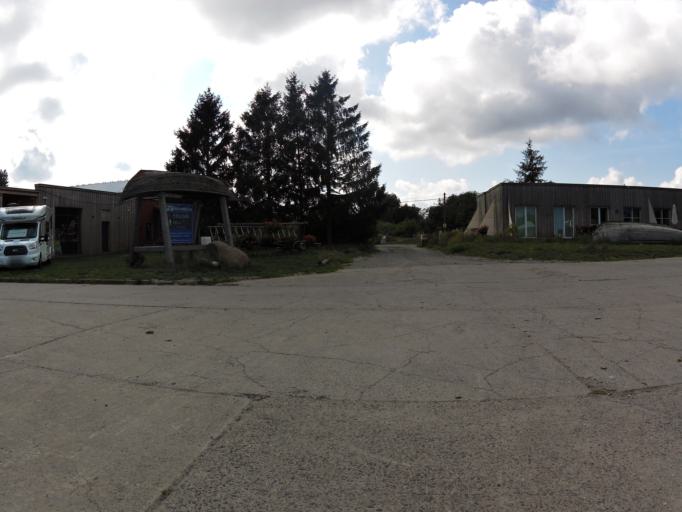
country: DE
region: Mecklenburg-Vorpommern
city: Kroslin
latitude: 54.1374
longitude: 13.7616
